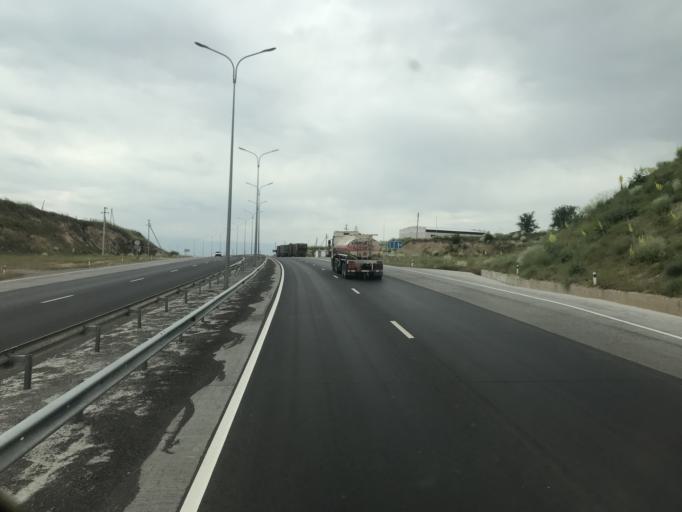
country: KZ
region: Ongtustik Qazaqstan
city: Qazyqurt
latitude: 41.9968
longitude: 69.4768
